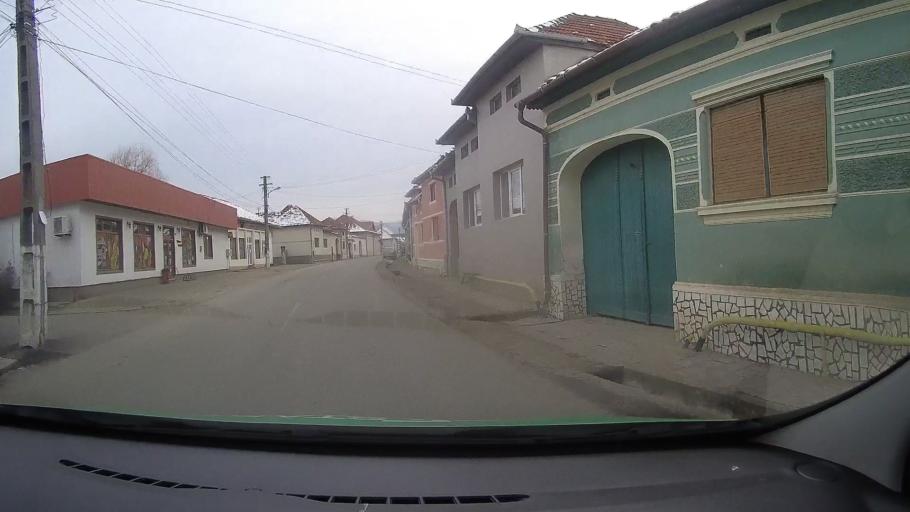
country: RO
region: Hunedoara
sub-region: Comuna Romos
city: Romos
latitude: 45.8424
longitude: 23.2745
